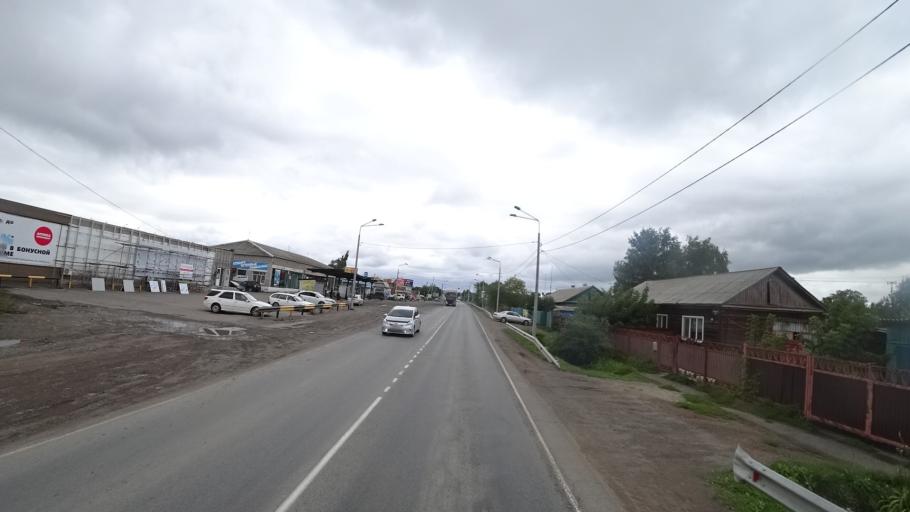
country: RU
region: Primorskiy
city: Chernigovka
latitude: 44.3403
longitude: 132.5878
